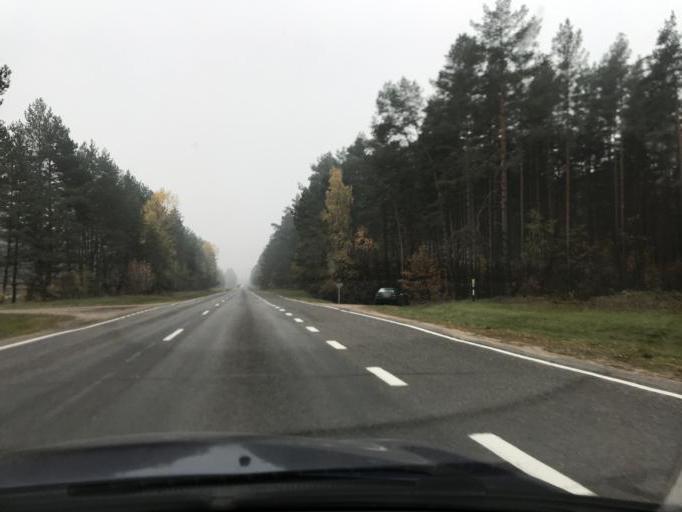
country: BY
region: Grodnenskaya
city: Hrodna
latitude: 53.7964
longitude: 23.8564
